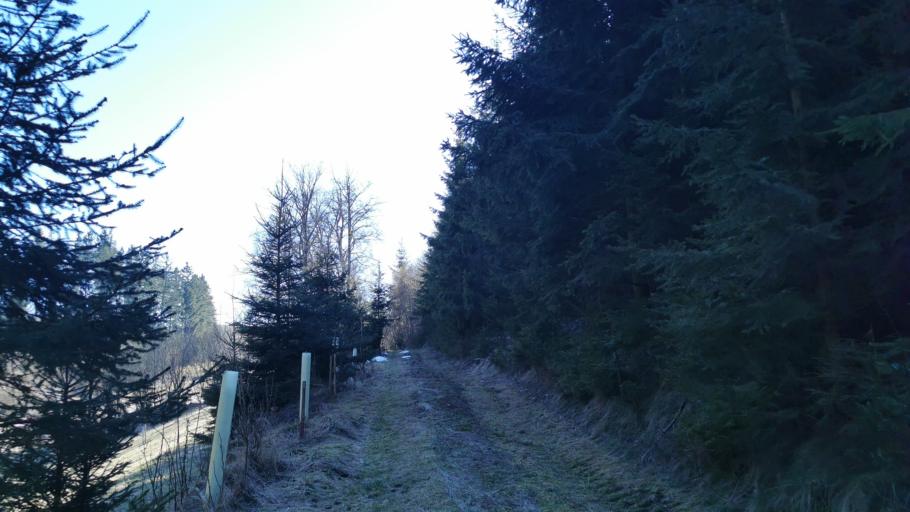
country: DE
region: Bavaria
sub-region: Upper Franconia
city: Ludwigsstadt
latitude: 50.4934
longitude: 11.4495
